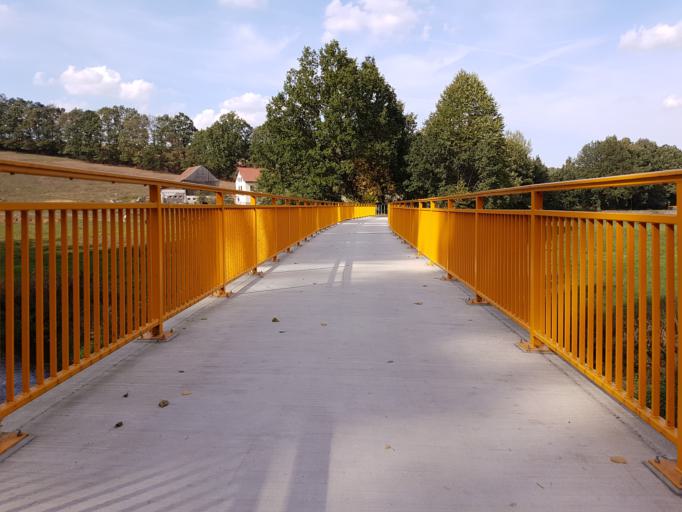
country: DE
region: Saxony
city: Claussnitz
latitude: 50.9049
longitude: 12.8952
